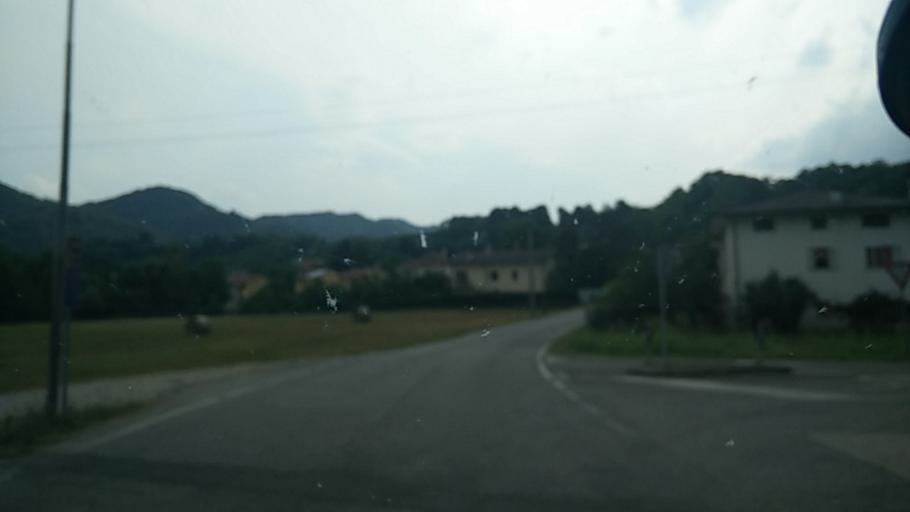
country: IT
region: Veneto
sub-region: Provincia di Treviso
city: Follina
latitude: 45.9393
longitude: 12.1302
